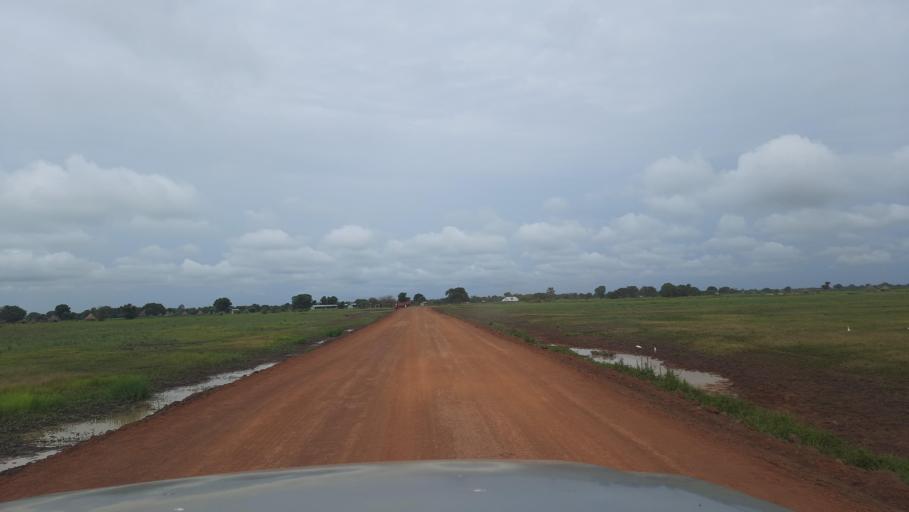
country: ET
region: Gambela
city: Gambela
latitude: 8.3331
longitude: 33.7739
